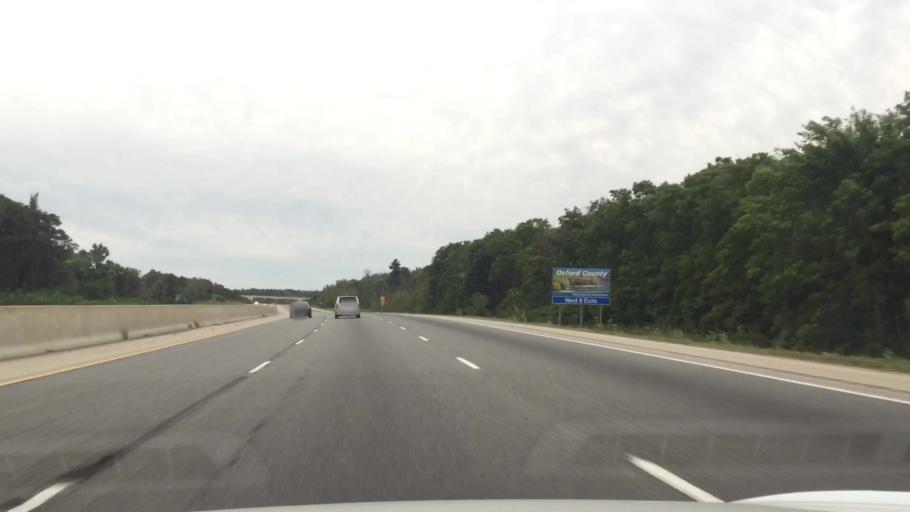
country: CA
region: Ontario
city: Kitchener
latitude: 43.2657
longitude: -80.5554
